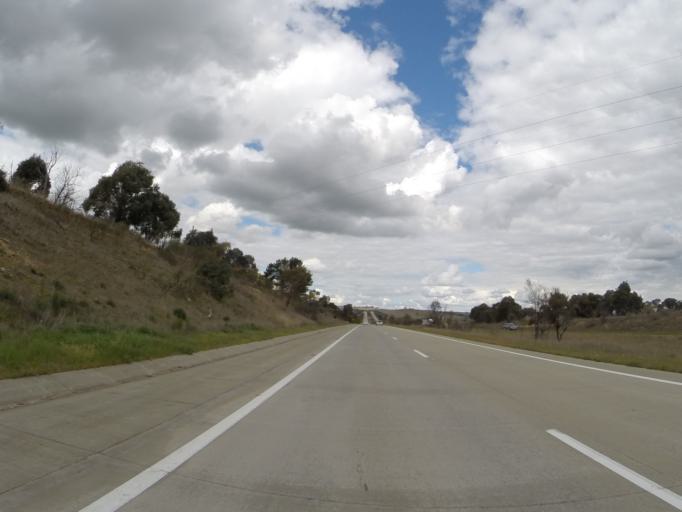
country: AU
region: New South Wales
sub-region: Yass Valley
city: Gundaroo
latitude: -34.7869
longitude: 149.2573
